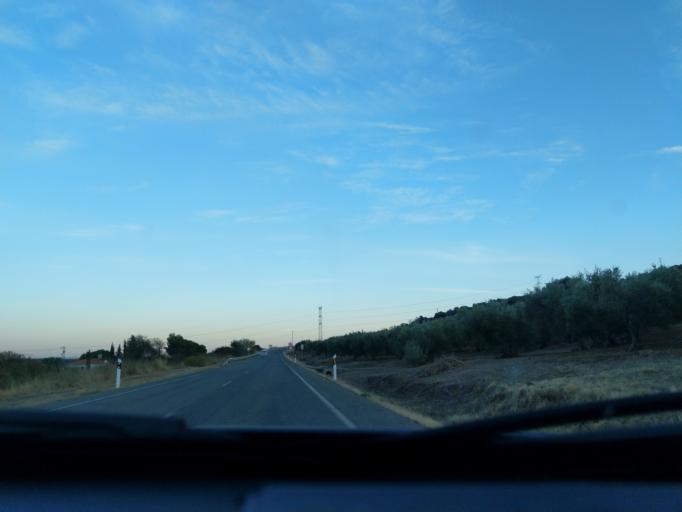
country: ES
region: Extremadura
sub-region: Provincia de Badajoz
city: Reina
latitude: 38.1858
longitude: -5.9366
